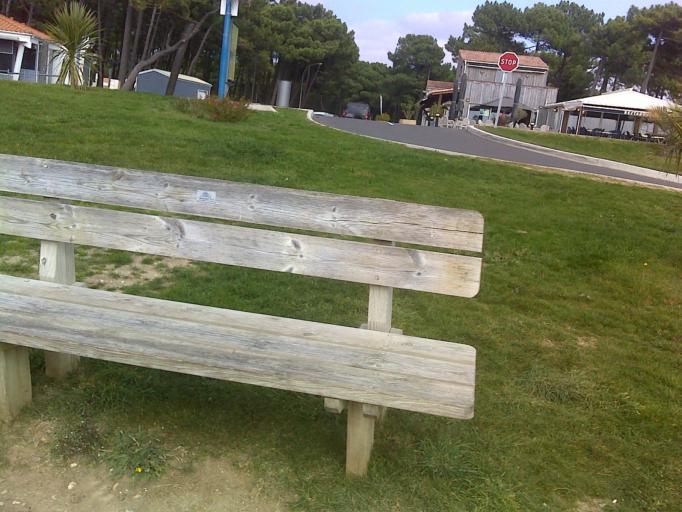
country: FR
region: Poitou-Charentes
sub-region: Departement de la Charente-Maritime
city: Les Mathes
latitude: 45.6841
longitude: -1.1820
